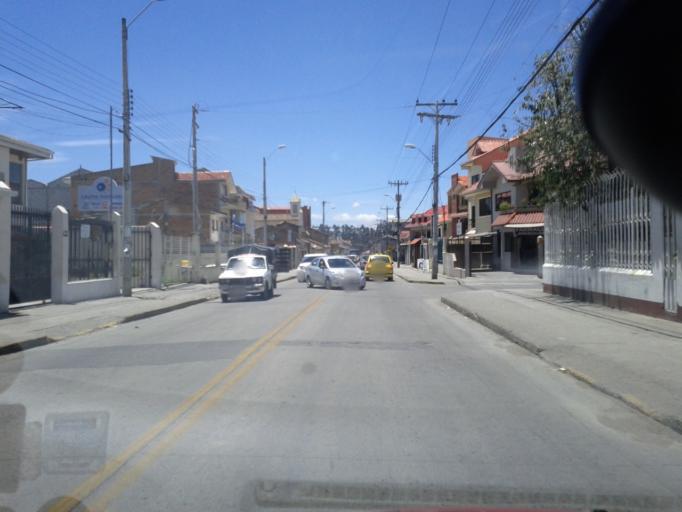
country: EC
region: Azuay
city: Cuenca
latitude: -2.9126
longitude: -79.0303
